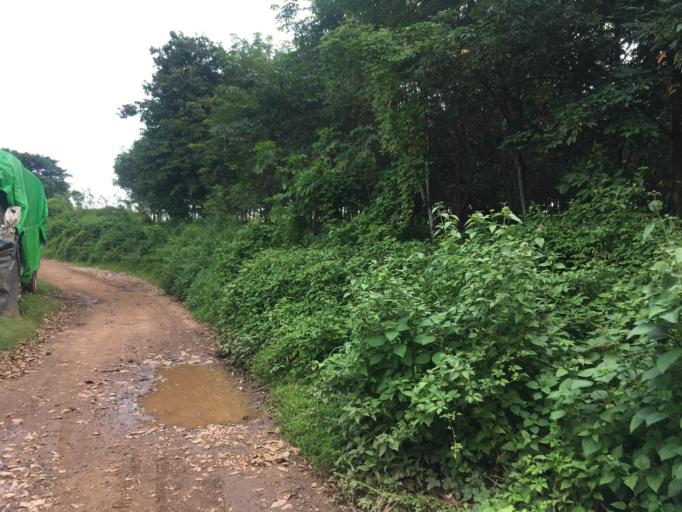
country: MM
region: Mon
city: Mawlamyine
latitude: 16.4591
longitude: 97.6655
